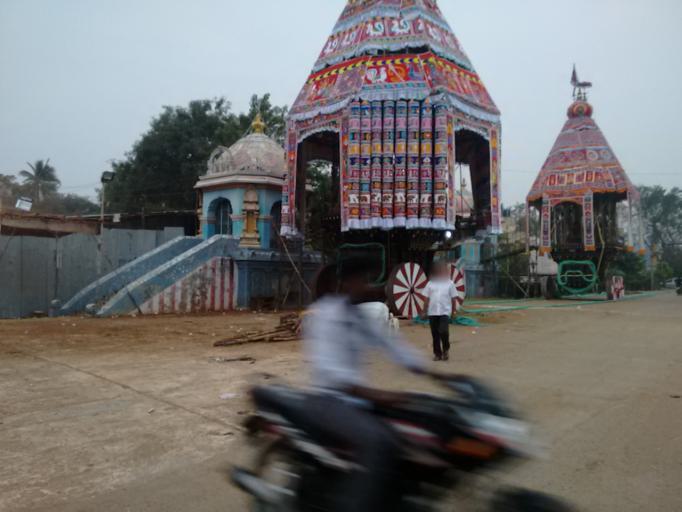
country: IN
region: Tamil Nadu
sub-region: Thanjavur
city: Thiruvidaimaruthur
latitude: 10.9963
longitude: 79.4557
